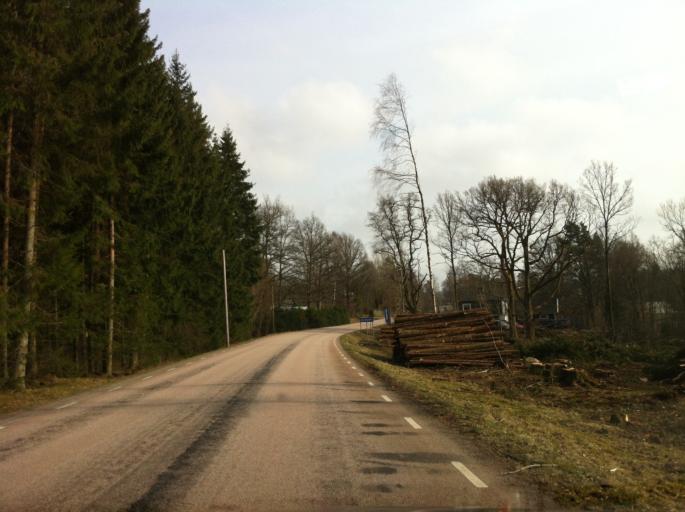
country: SE
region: Vaestra Goetaland
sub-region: Boras Kommun
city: Dalsjofors
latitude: 57.8270
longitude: 13.0224
